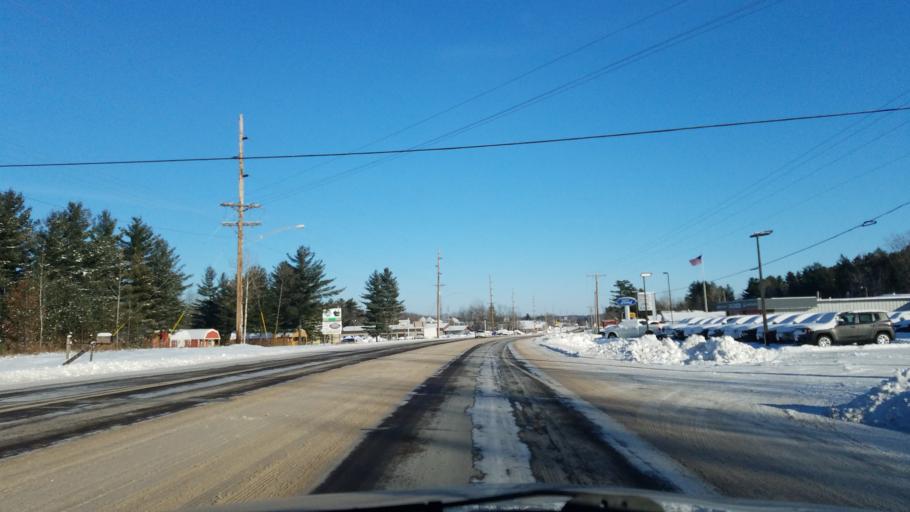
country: US
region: Wisconsin
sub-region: Barron County
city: Cumberland
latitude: 45.5309
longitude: -92.0420
